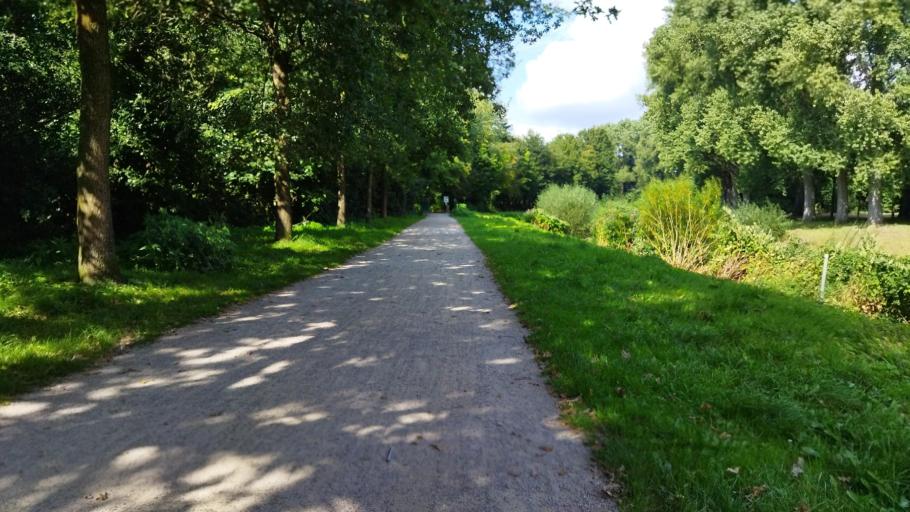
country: DE
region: North Rhine-Westphalia
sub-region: Regierungsbezirk Munster
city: Telgte
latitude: 51.9866
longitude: 7.7856
